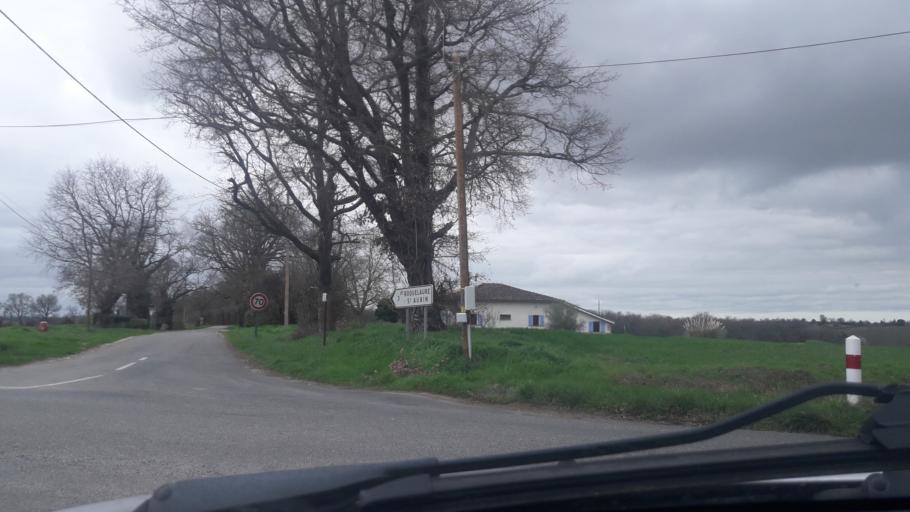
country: FR
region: Midi-Pyrenees
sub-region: Departement du Gers
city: Gimont
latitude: 43.6550
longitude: 1.0090
